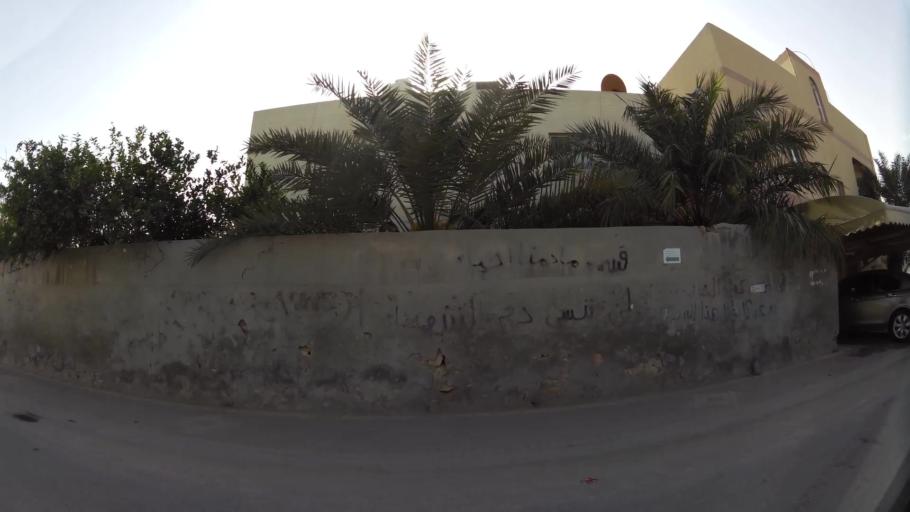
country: BH
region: Manama
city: Jidd Hafs
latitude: 26.2125
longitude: 50.5132
